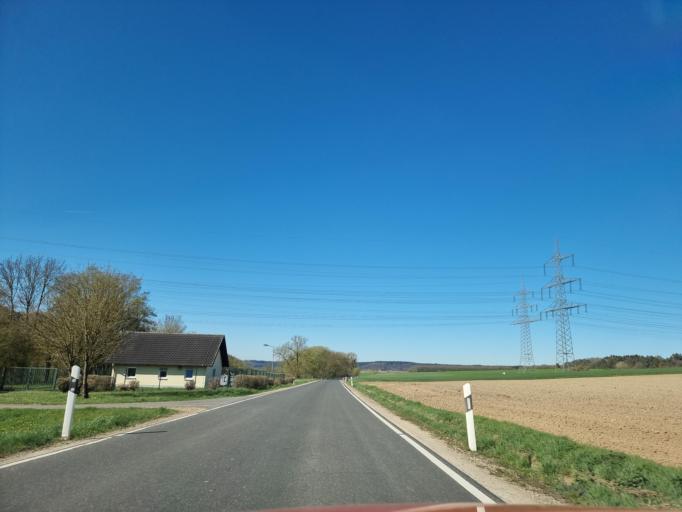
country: DE
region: Rheinland-Pfalz
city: Meckel
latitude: 49.8879
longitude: 6.5103
